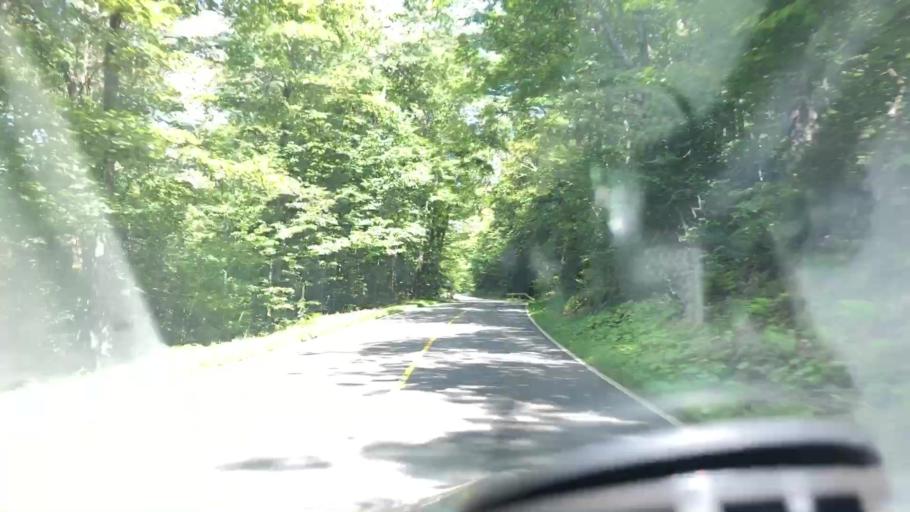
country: US
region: Massachusetts
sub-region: Berkshire County
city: Adams
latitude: 42.6140
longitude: -73.2000
